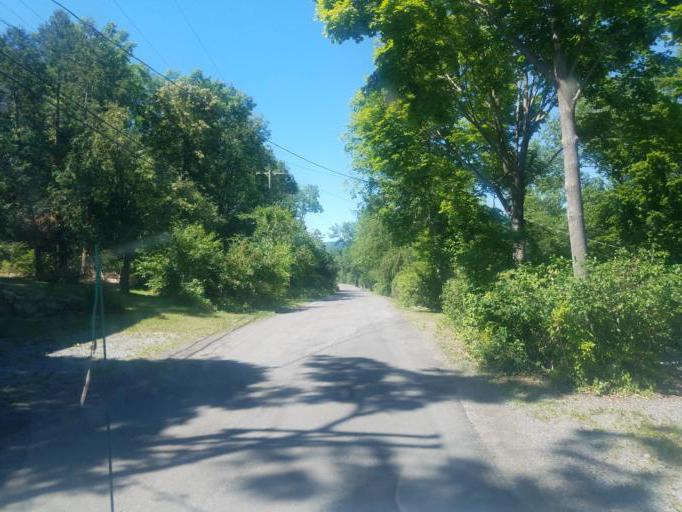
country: US
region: New York
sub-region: Ontario County
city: Naples
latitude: 42.7184
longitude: -77.3311
